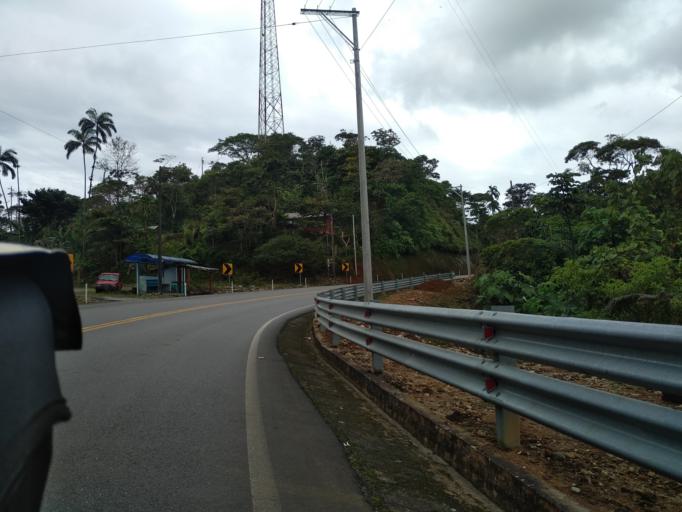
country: EC
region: Pastaza
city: Puyo
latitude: -1.3051
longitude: -77.8829
